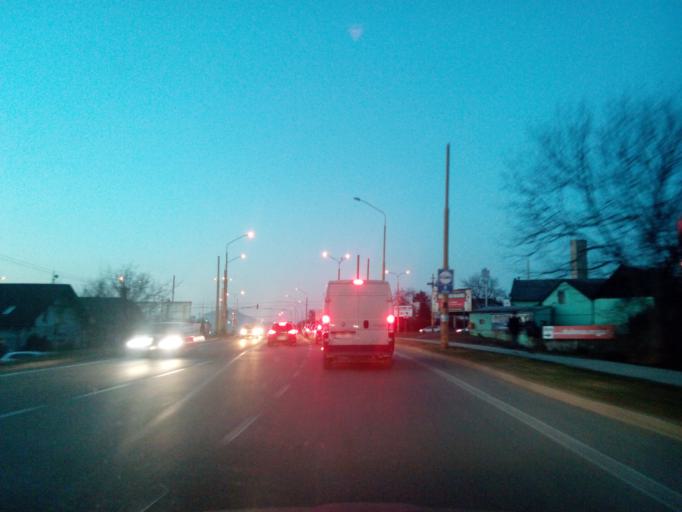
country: SK
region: Presovsky
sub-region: Okres Presov
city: Presov
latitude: 48.9767
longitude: 21.2640
